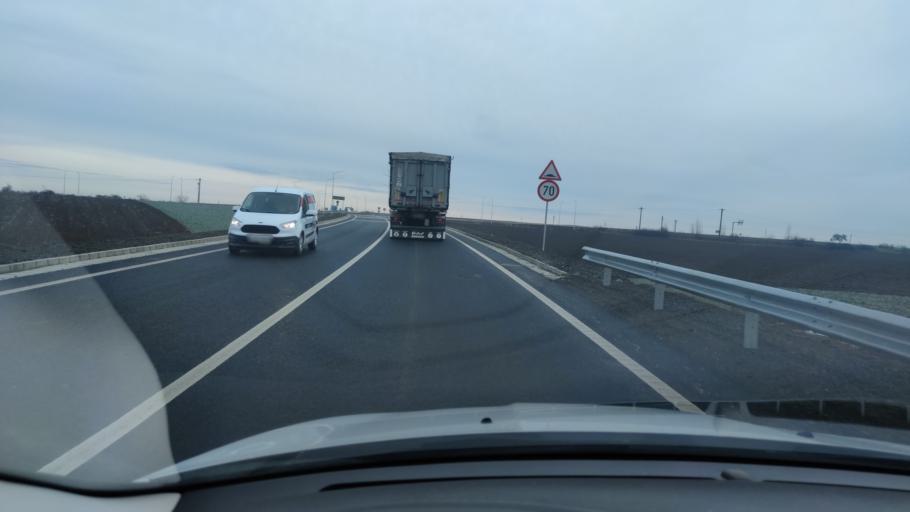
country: RO
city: Szekelyhid
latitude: 47.3507
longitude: 22.1280
